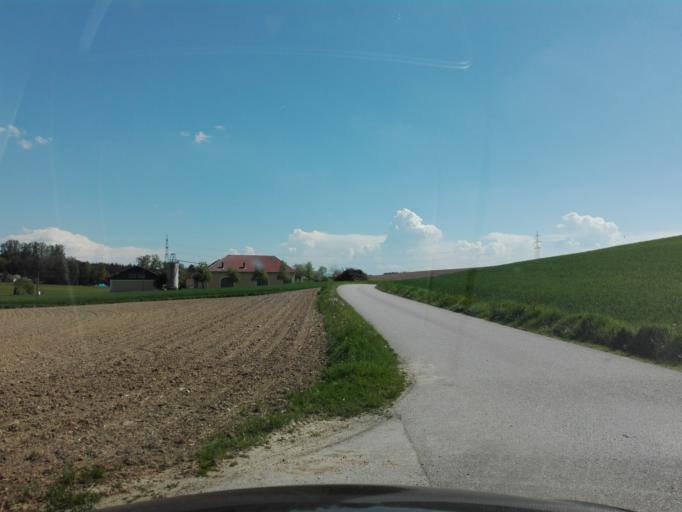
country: AT
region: Upper Austria
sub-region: Politischer Bezirk Grieskirchen
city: Bad Schallerbach
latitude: 48.3457
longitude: 13.8923
